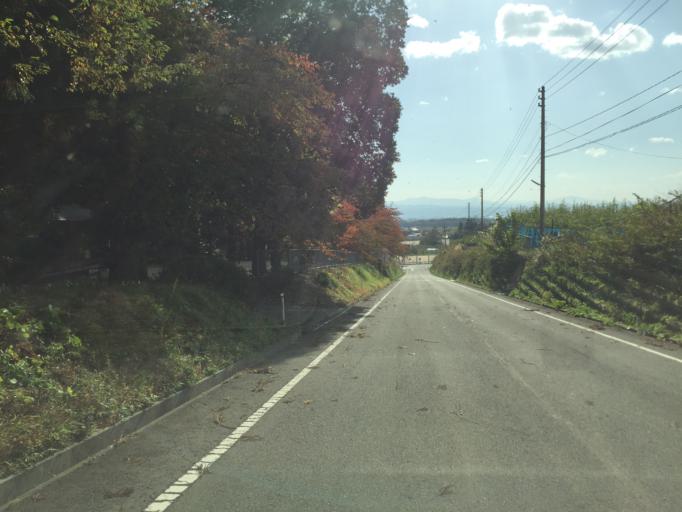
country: JP
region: Fukushima
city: Fukushima-shi
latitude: 37.7959
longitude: 140.3907
